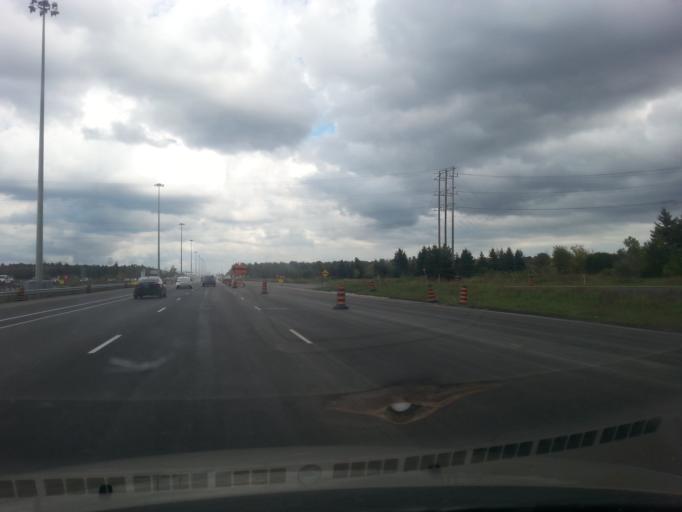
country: CA
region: Ontario
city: Bells Corners
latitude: 45.3211
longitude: -75.8836
